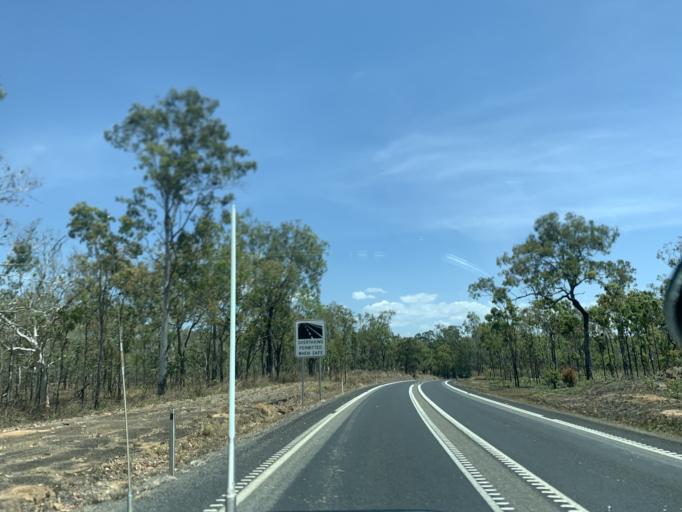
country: AU
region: Queensland
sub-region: Tablelands
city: Mareeba
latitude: -16.9398
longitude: 145.5429
